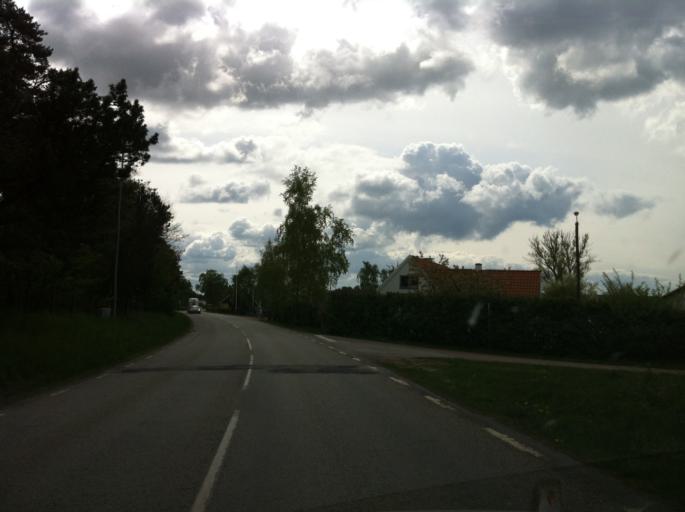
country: SE
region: Skane
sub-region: Kavlinge Kommun
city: Hofterup
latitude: 55.8321
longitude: 12.9627
